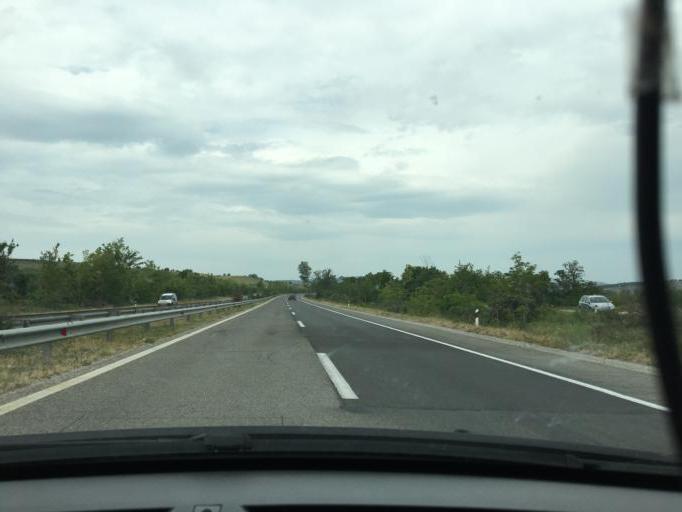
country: MK
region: Gradsko
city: Gradsko
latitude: 41.6001
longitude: 21.9107
